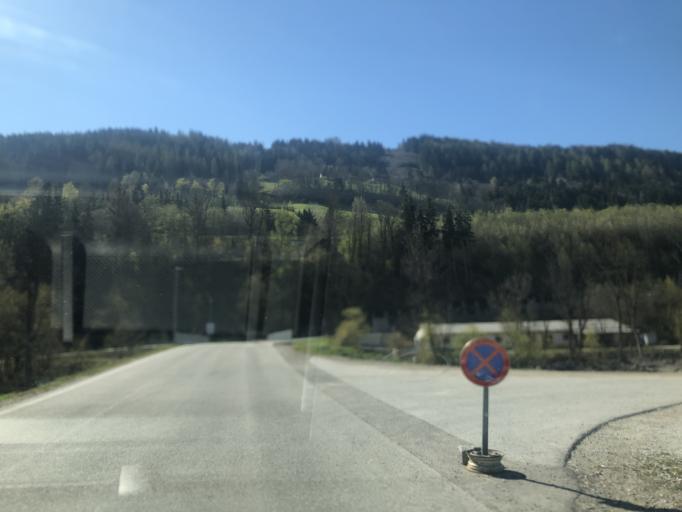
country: AT
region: Styria
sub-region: Politischer Bezirk Liezen
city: Schladming
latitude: 47.3998
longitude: 13.7058
